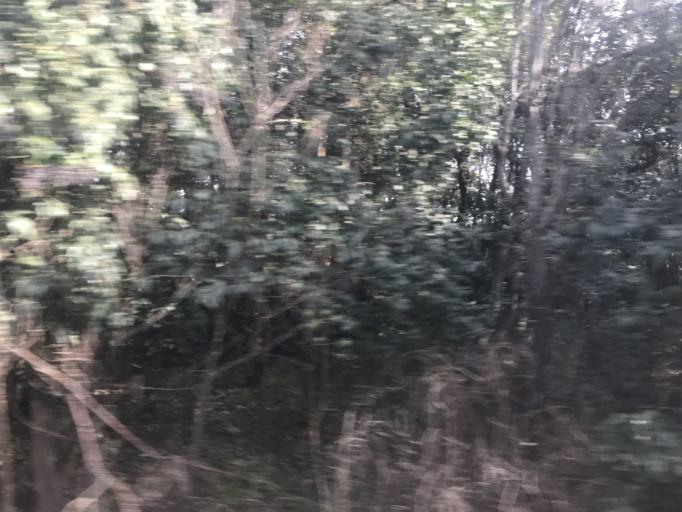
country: AR
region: Cordoba
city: Laguna Larga
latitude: -31.7875
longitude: -63.7940
